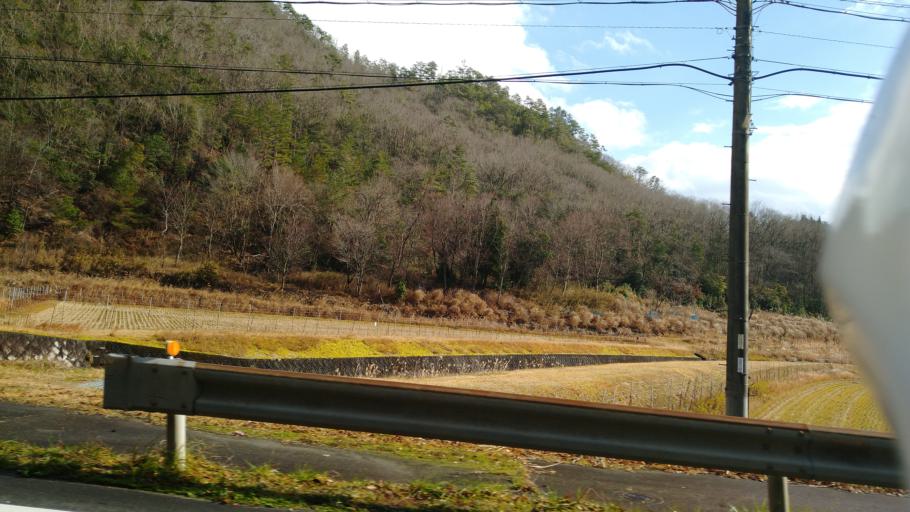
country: JP
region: Hyogo
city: Sasayama
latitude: 35.1298
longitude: 135.3338
